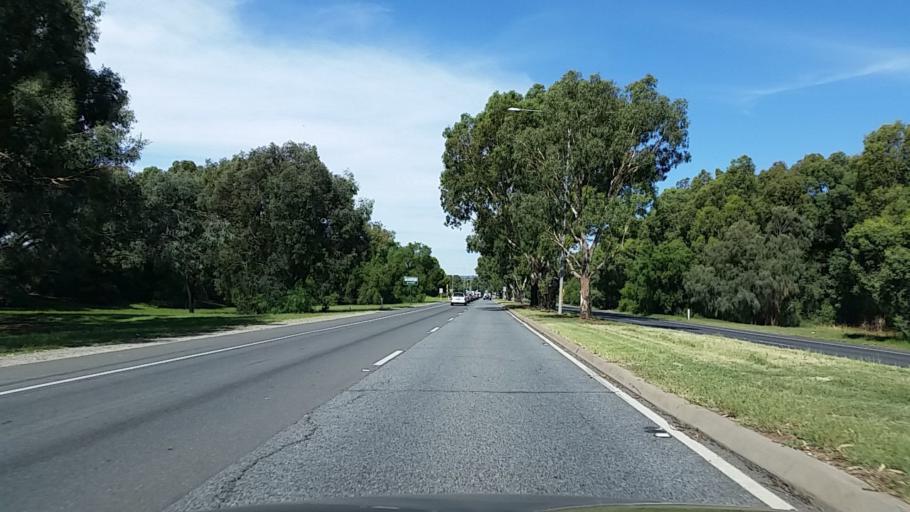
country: AU
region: South Australia
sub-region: Salisbury
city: Ingle Farm
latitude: -34.8255
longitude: 138.6105
